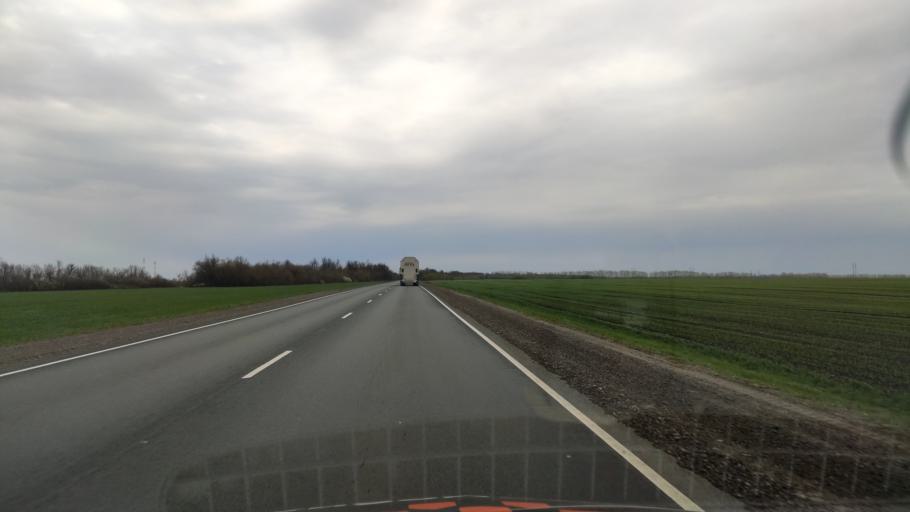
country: RU
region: Voronezj
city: Nizhnedevitsk
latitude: 51.6044
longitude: 38.6055
